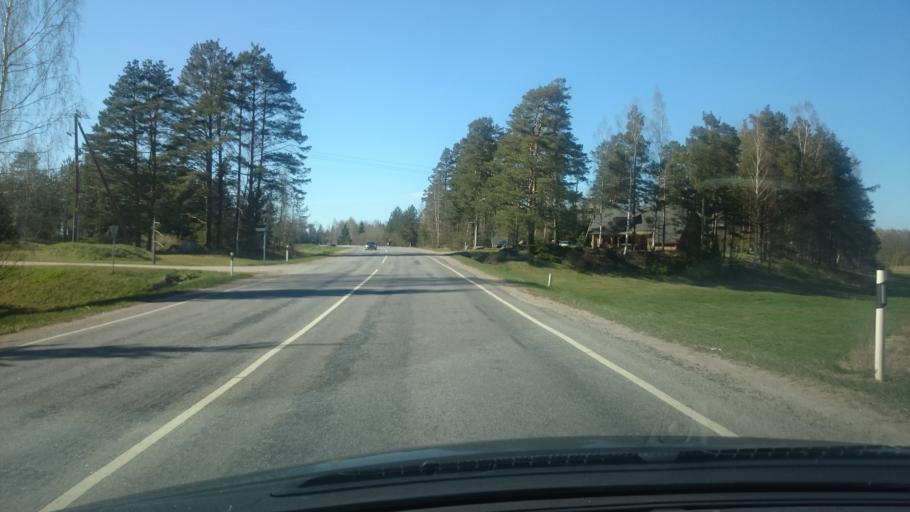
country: EE
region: Tartu
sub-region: UElenurme vald
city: Ulenurme
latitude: 58.3333
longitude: 26.9774
